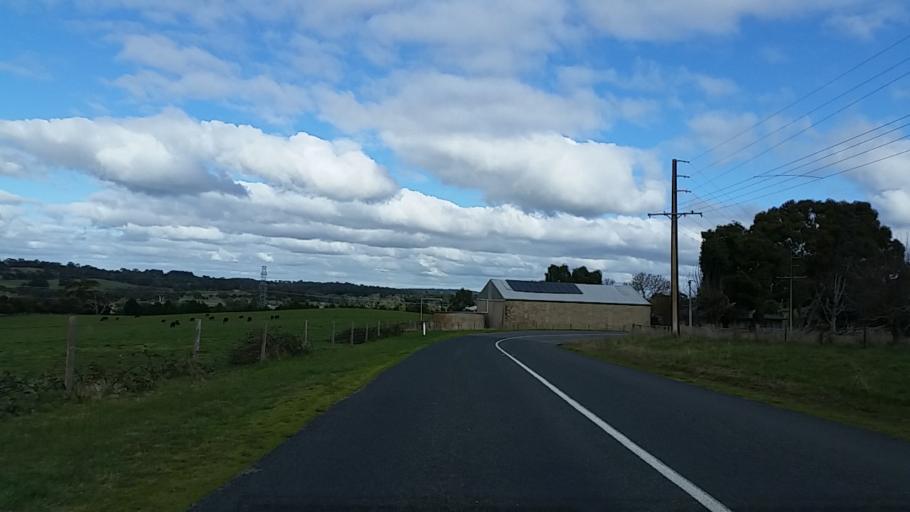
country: AU
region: South Australia
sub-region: Mount Barker
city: Little Hampton
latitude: -35.0765
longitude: 138.8339
